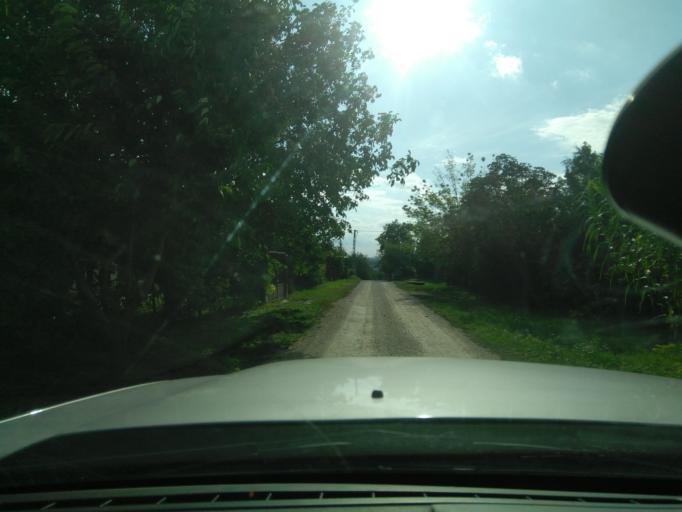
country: HU
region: Fejer
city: Bicske
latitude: 47.5000
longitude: 18.6594
